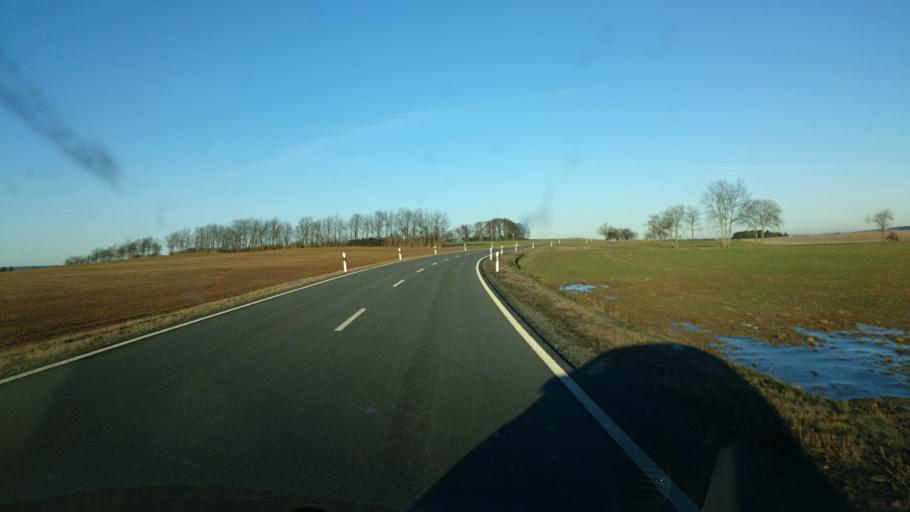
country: DE
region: Thuringia
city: Kirschkau
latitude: 50.5930
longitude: 11.8868
